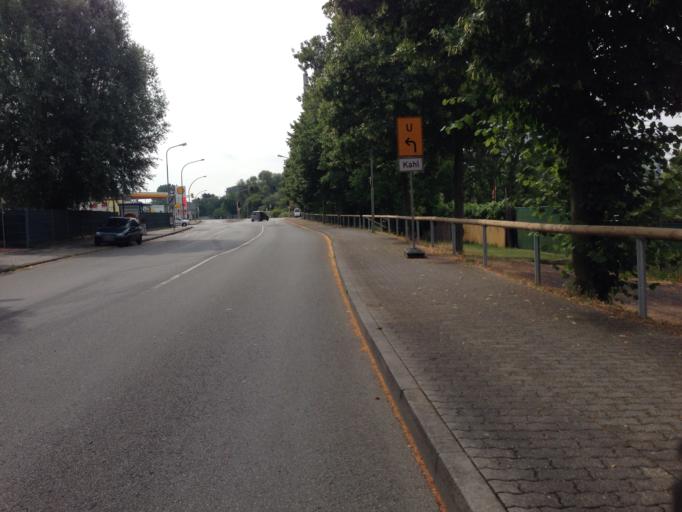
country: DE
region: Hesse
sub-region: Regierungsbezirk Darmstadt
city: Grosskrotzenburg
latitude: 50.0956
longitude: 8.9482
